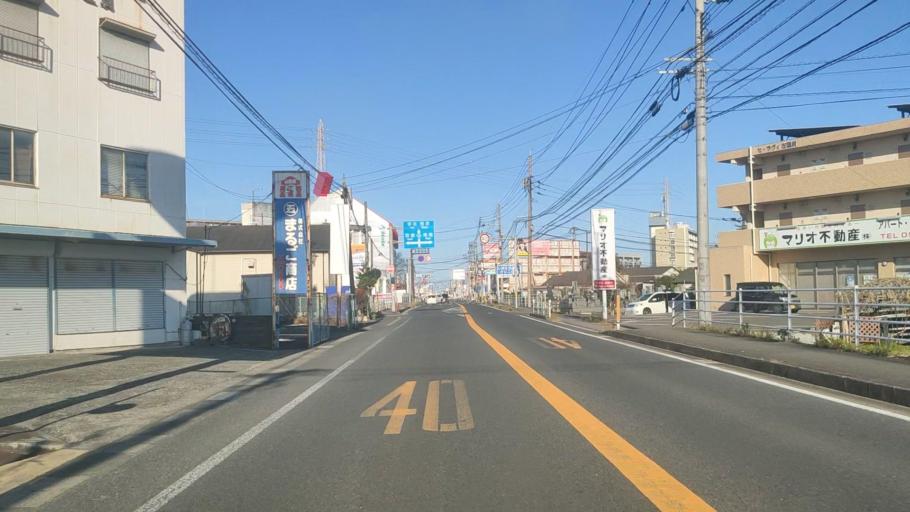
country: JP
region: Oita
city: Oita
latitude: 33.2156
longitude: 131.6119
